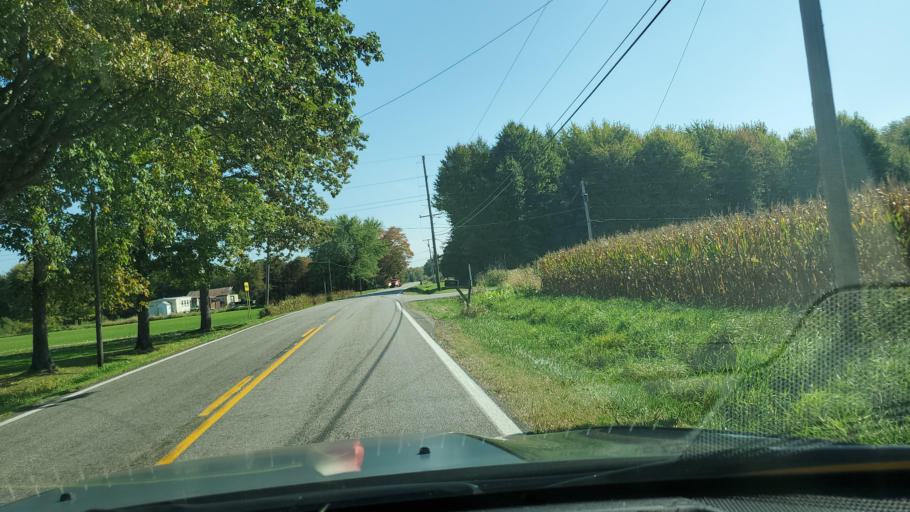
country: US
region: Ohio
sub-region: Trumbull County
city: Cortland
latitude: 41.3885
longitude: -80.6188
